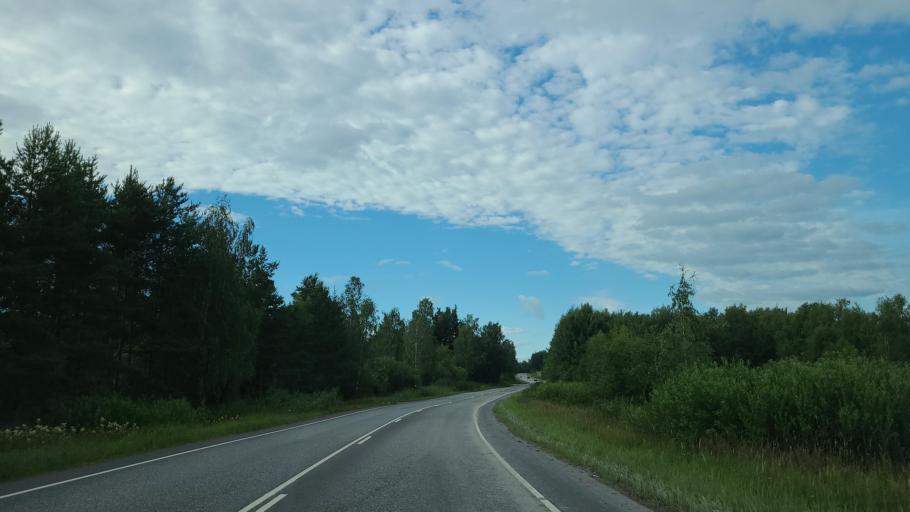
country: FI
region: Varsinais-Suomi
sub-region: Turku
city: Merimasku
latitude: 60.4301
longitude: 21.8949
